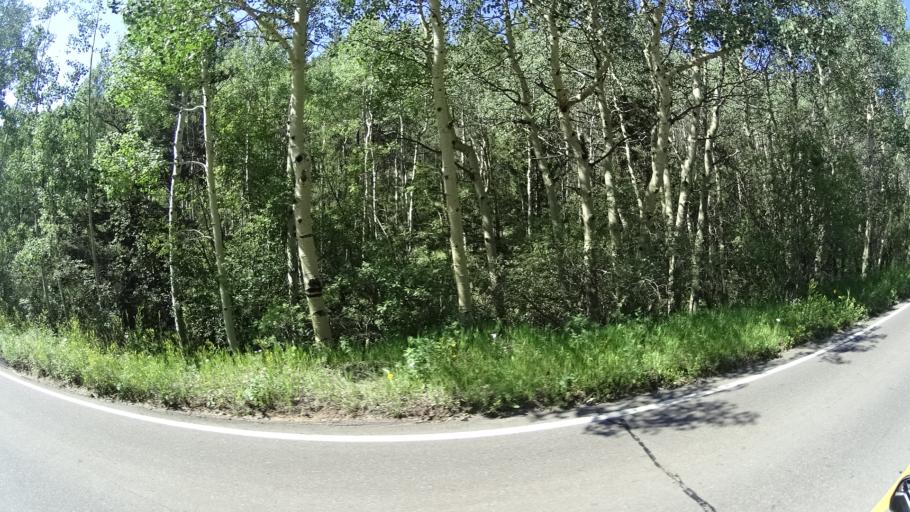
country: US
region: Colorado
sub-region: El Paso County
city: Cascade-Chipita Park
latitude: 38.9023
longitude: -105.0037
